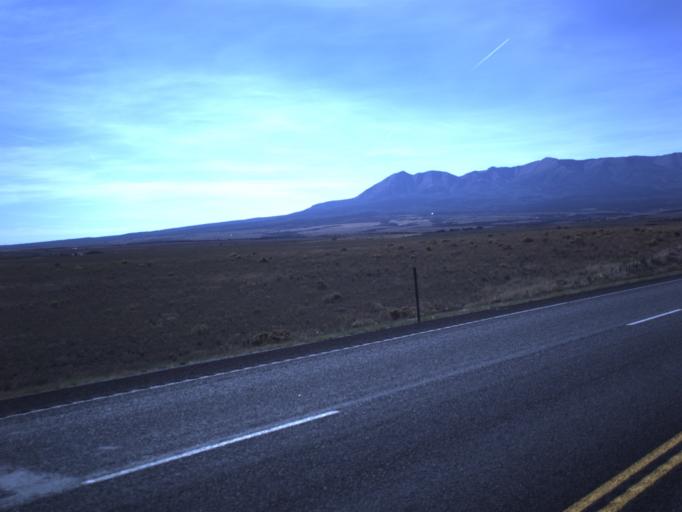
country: US
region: Utah
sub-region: San Juan County
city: Monticello
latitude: 37.8658
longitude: -109.2326
